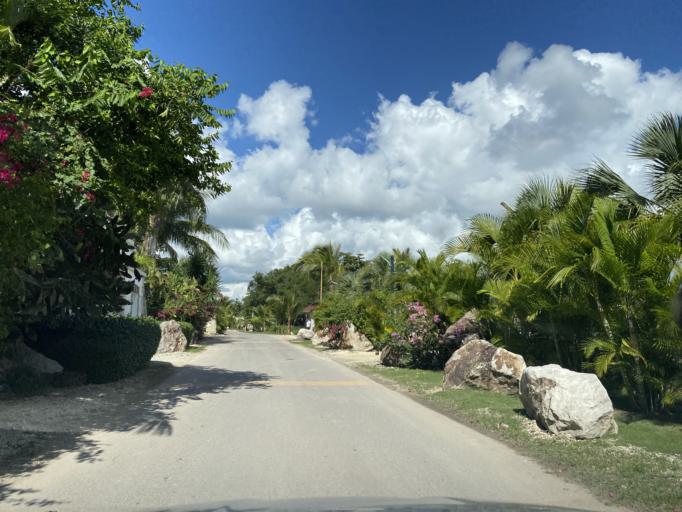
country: DO
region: La Romana
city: La Romana
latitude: 18.3515
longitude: -68.8333
